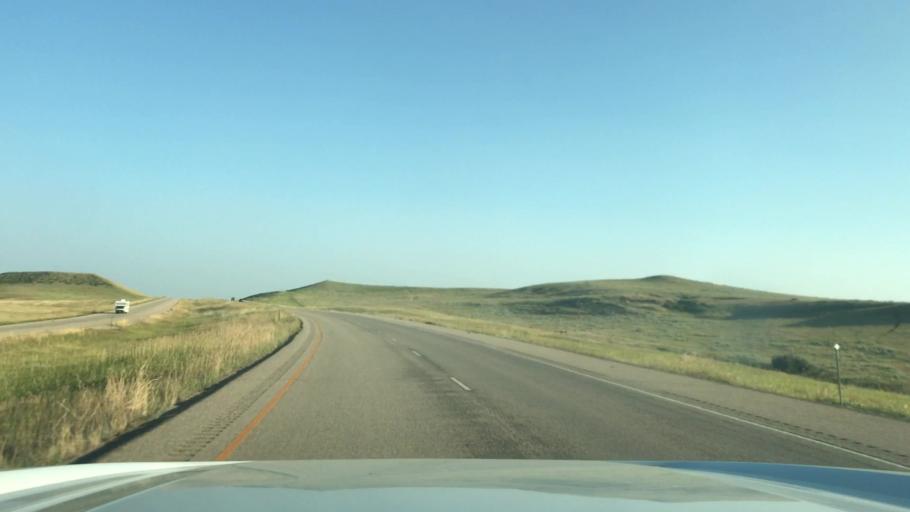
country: US
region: Montana
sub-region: Big Horn County
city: Crow Agency
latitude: 45.2306
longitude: -107.3641
